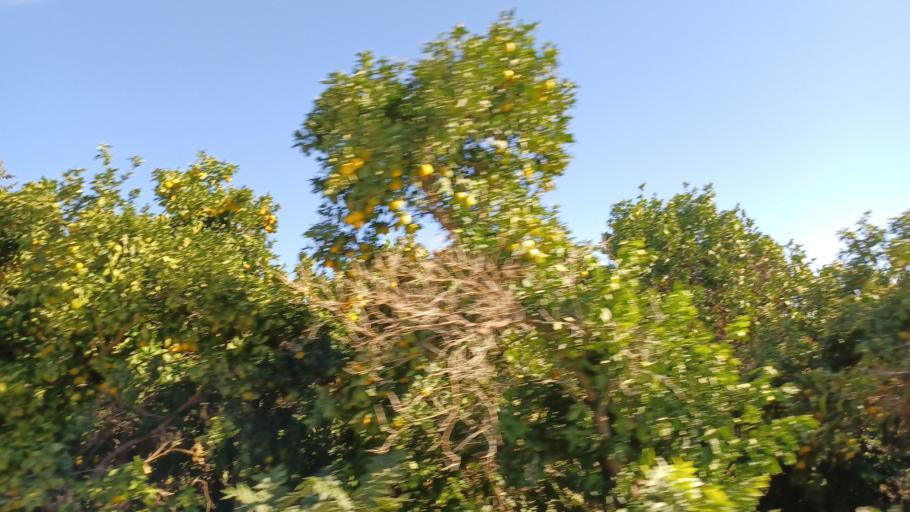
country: CY
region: Pafos
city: Polis
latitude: 35.0256
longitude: 32.4216
